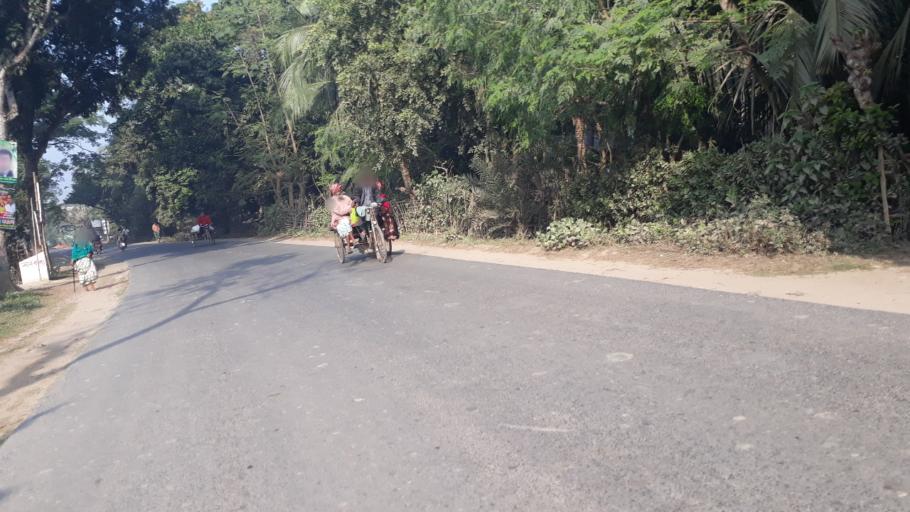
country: BD
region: Khulna
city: Kaliganj
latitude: 23.4132
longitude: 89.0148
